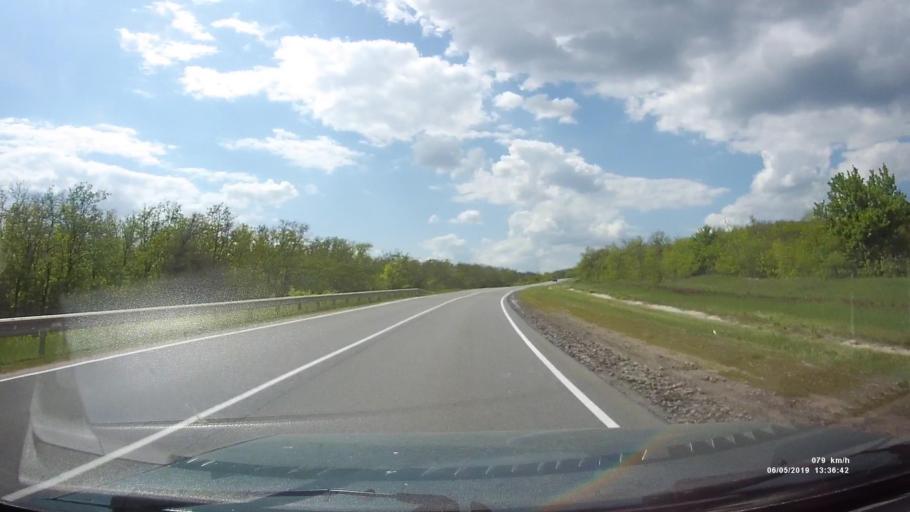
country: RU
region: Rostov
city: Ust'-Donetskiy
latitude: 47.6893
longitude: 40.7281
